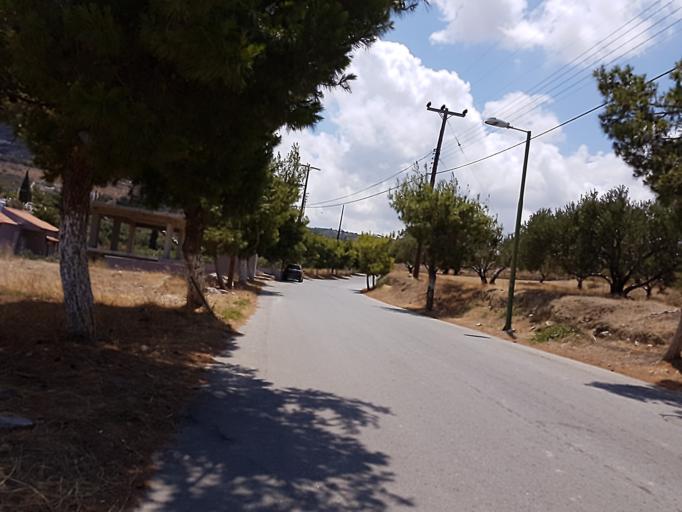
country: GR
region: Crete
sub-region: Nomos Irakleiou
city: Limin Khersonisou
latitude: 35.3125
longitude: 25.3772
